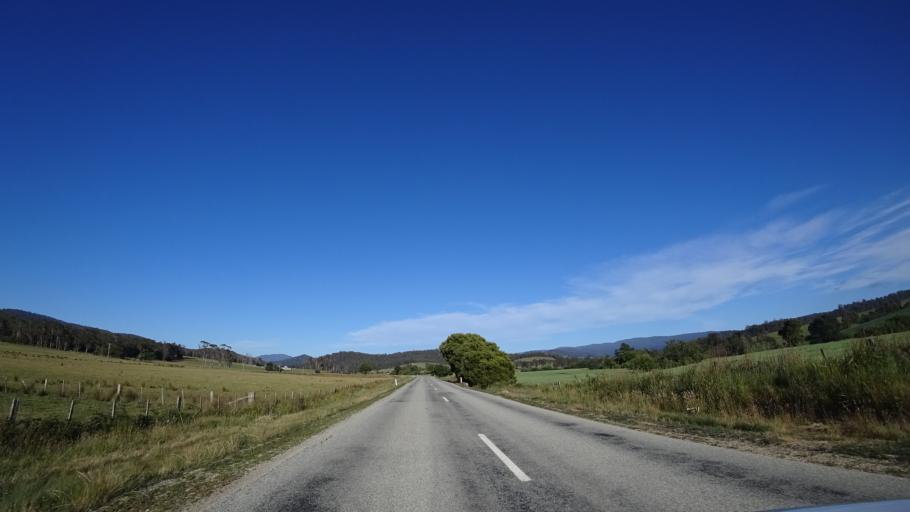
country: AU
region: Tasmania
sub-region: Break O'Day
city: St Helens
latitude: -41.2722
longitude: 148.1083
